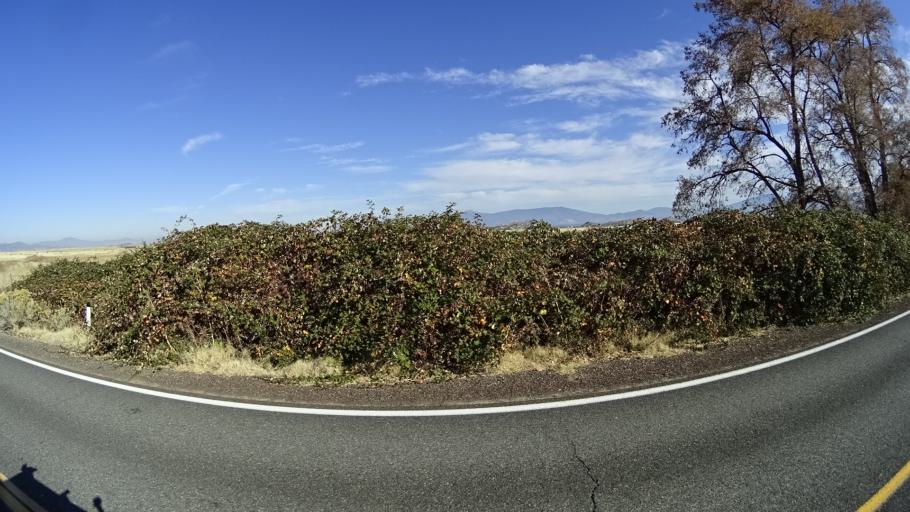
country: US
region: California
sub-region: Siskiyou County
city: Weed
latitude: 41.4693
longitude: -122.4735
